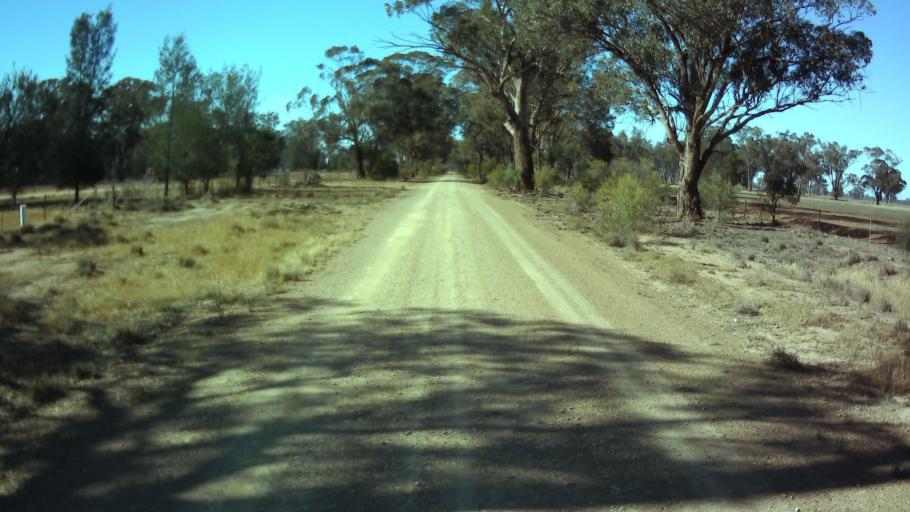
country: AU
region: New South Wales
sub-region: Weddin
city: Grenfell
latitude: -33.9367
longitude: 147.8718
